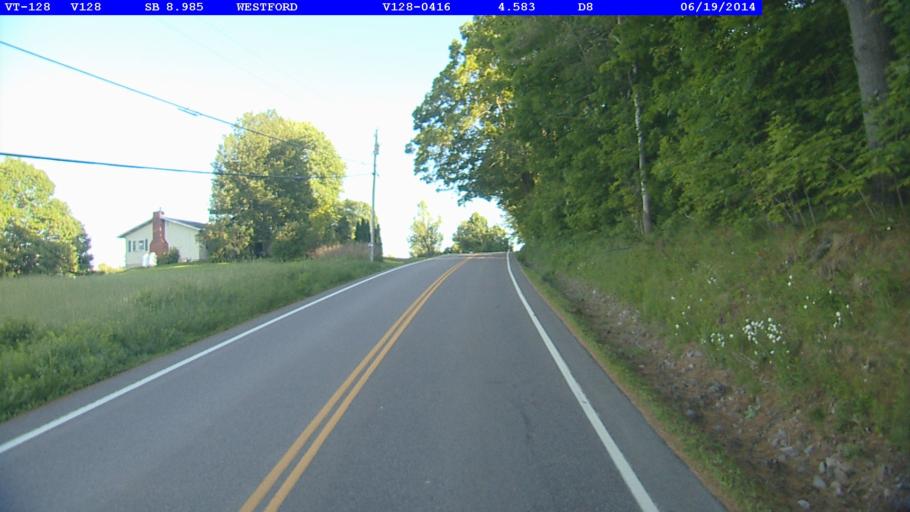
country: US
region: Vermont
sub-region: Chittenden County
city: Milton
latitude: 44.6204
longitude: -73.0157
